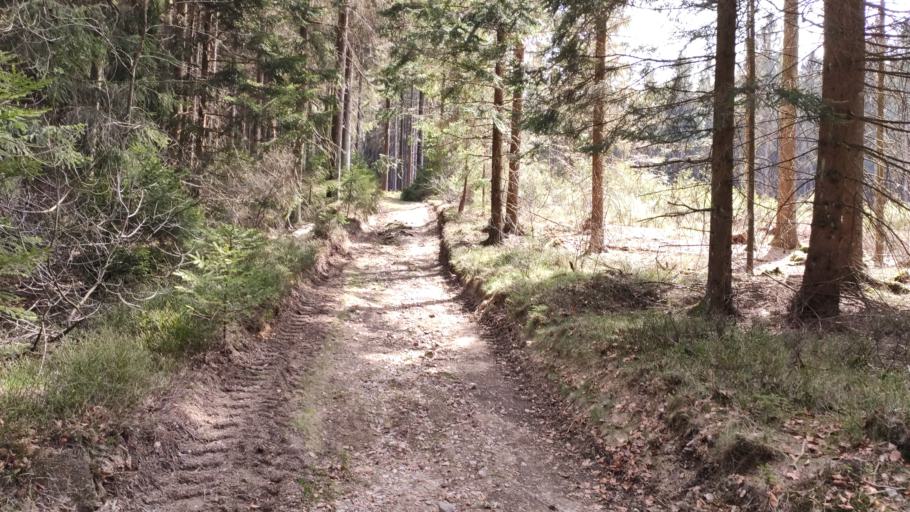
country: DE
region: Bavaria
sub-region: Upper Franconia
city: Reichenbach
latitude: 50.4517
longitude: 11.4489
